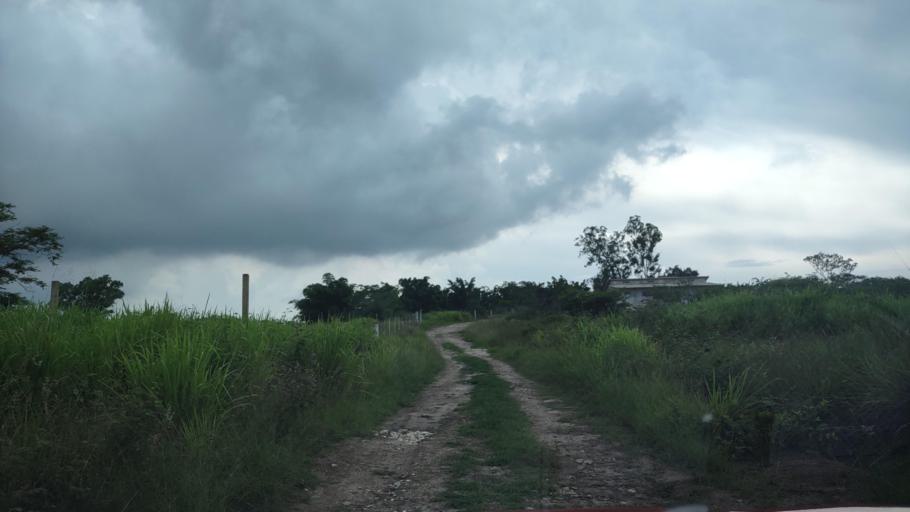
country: MX
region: Veracruz
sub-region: Emiliano Zapata
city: Dos Rios
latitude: 19.4760
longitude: -96.8169
